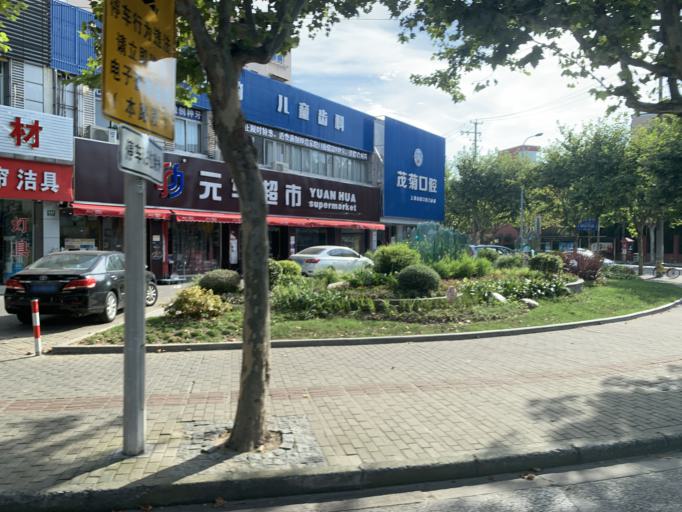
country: CN
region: Shanghai Shi
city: Huamu
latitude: 31.2053
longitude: 121.5387
